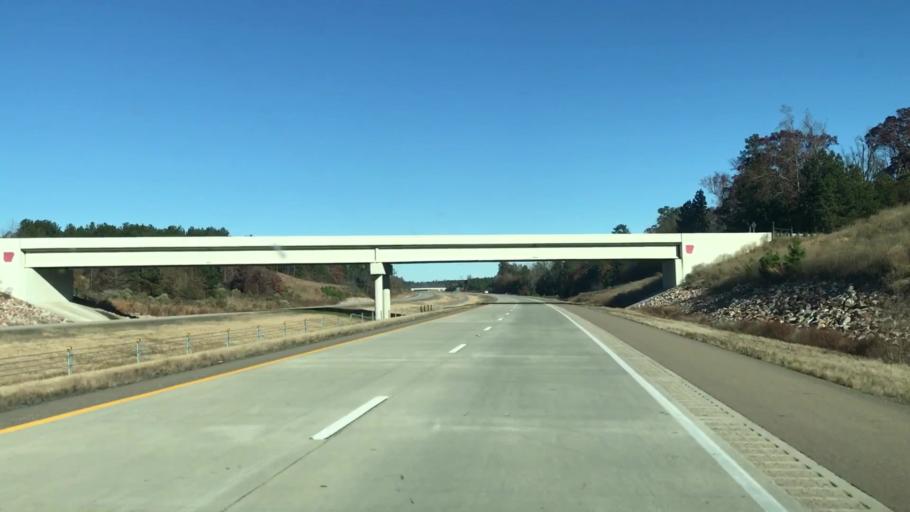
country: US
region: Louisiana
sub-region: Caddo Parish
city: Vivian
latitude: 33.0505
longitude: -93.9007
